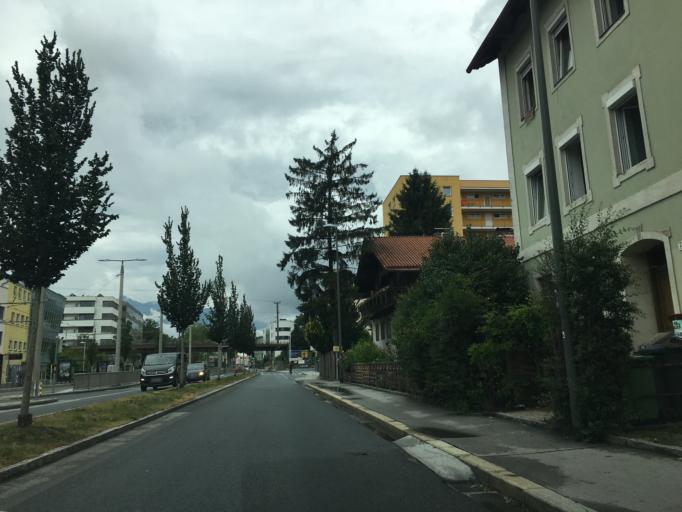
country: AT
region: Tyrol
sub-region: Innsbruck Stadt
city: Innsbruck
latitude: 47.2650
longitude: 11.3738
